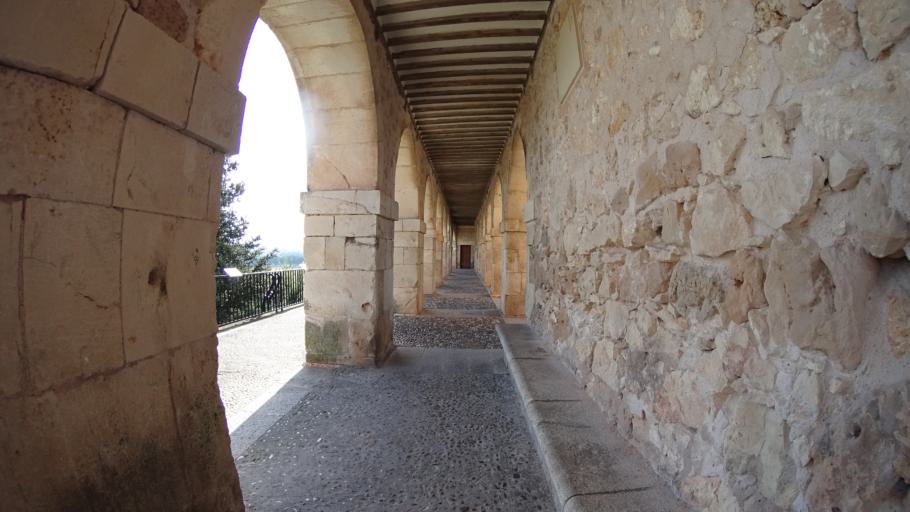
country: ES
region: Castille and Leon
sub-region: Provincia de Burgos
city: Lerma
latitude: 42.0271
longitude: -3.7576
